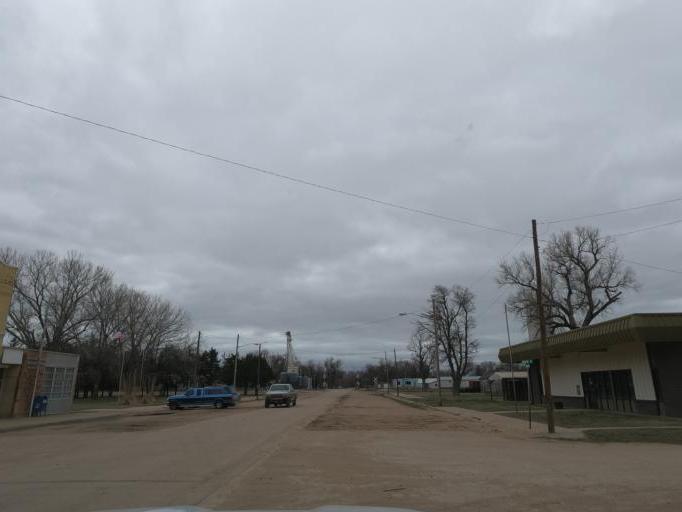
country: US
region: Kansas
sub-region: Stafford County
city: Stafford
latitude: 37.9590
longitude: -98.4085
